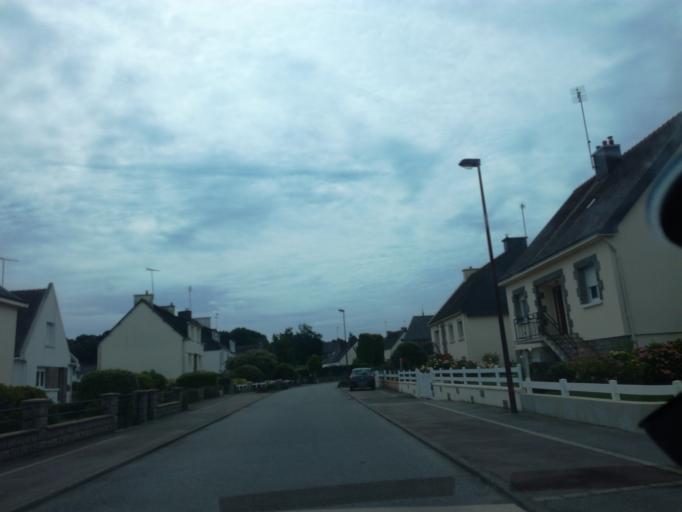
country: FR
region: Brittany
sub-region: Departement du Morbihan
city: Saint-Thuriau
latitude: 48.0193
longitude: -2.9519
